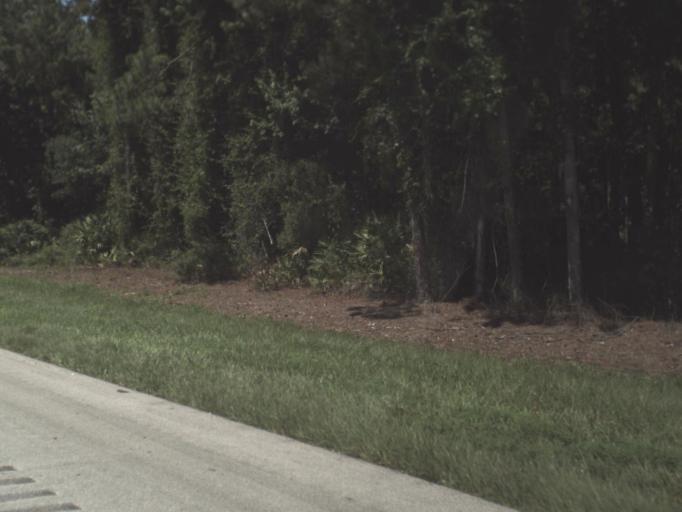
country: US
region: Florida
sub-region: Saint Johns County
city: Saint Augustine
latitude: 29.8711
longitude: -81.3981
